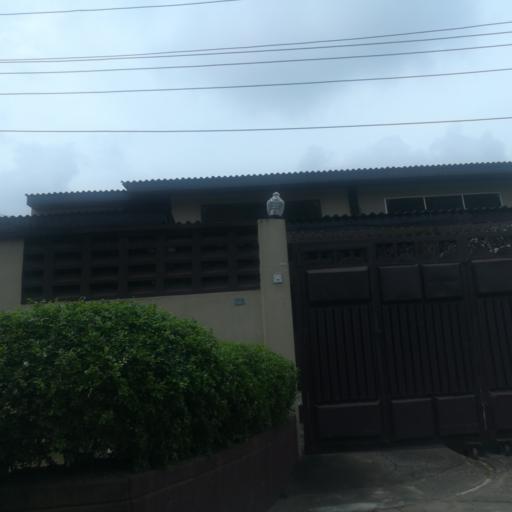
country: NG
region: Lagos
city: Ojota
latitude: 6.5764
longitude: 3.3924
